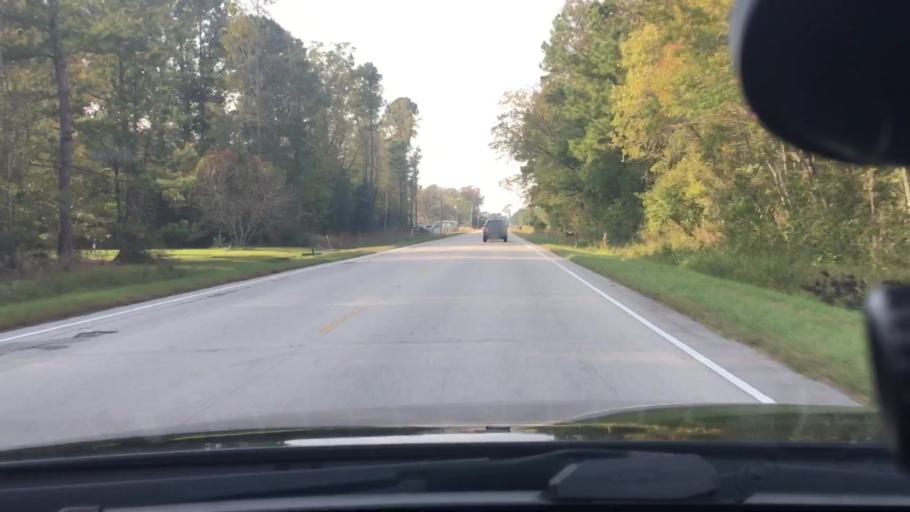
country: US
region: North Carolina
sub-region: Craven County
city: Vanceboro
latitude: 35.3474
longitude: -77.1842
